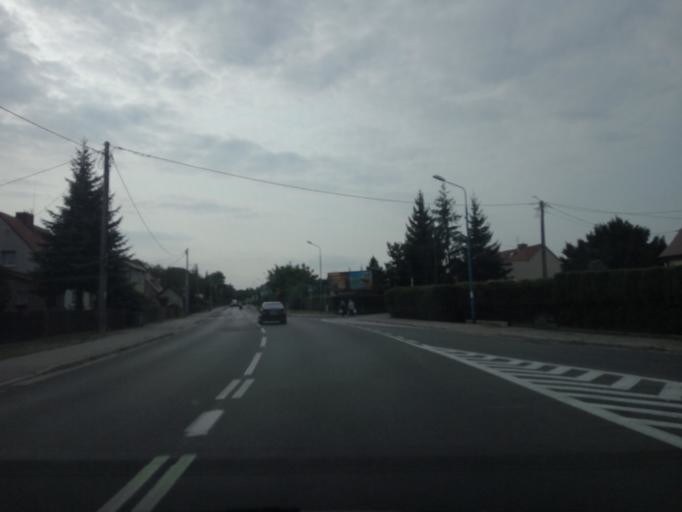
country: PL
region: Lower Silesian Voivodeship
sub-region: Powiat strzelinski
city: Strzelin
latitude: 50.7894
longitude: 17.0669
